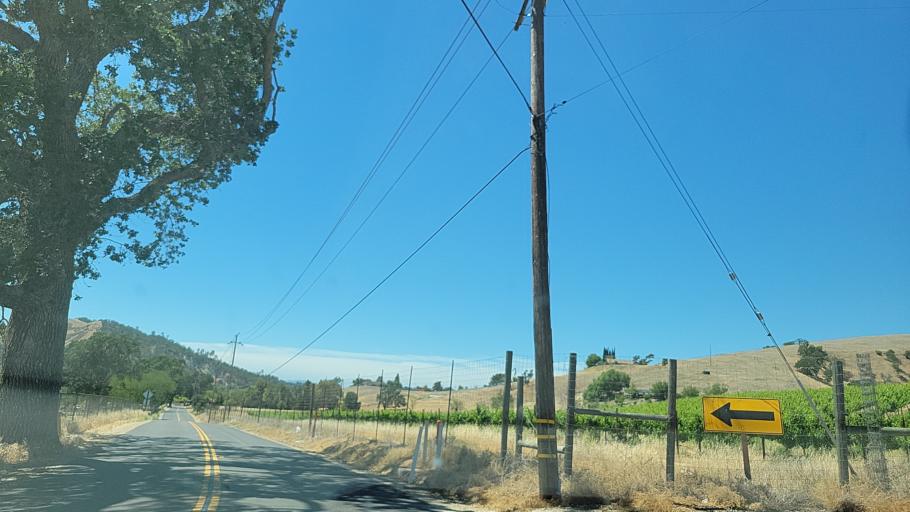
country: US
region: California
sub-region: San Luis Obispo County
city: Atascadero
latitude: 35.4865
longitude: -120.6333
